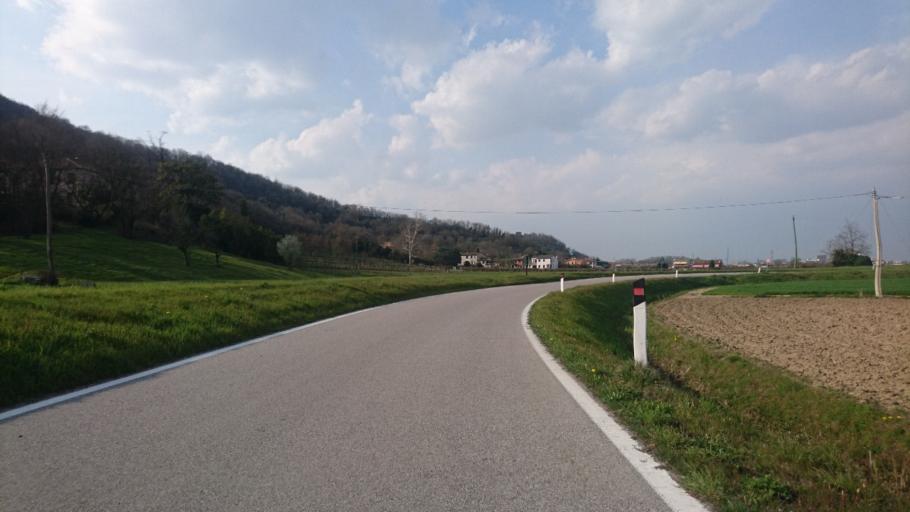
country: IT
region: Veneto
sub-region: Provincia di Padova
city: Battaglia Terme
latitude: 45.3047
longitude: 11.7916
